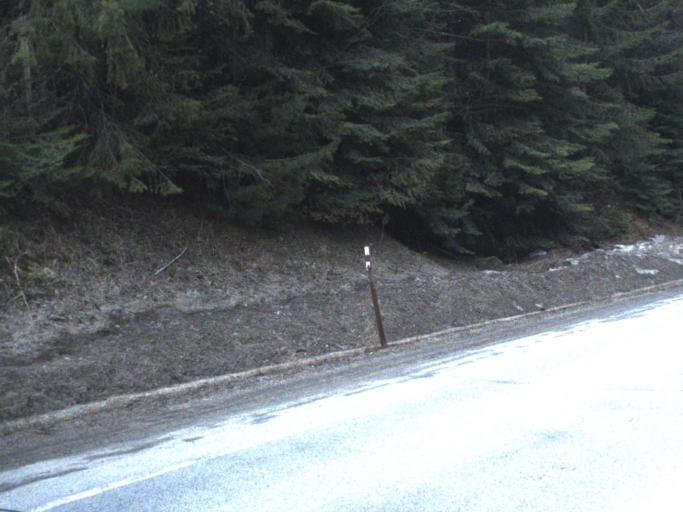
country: US
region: Washington
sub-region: Pend Oreille County
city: Newport
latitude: 48.2158
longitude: -117.0755
